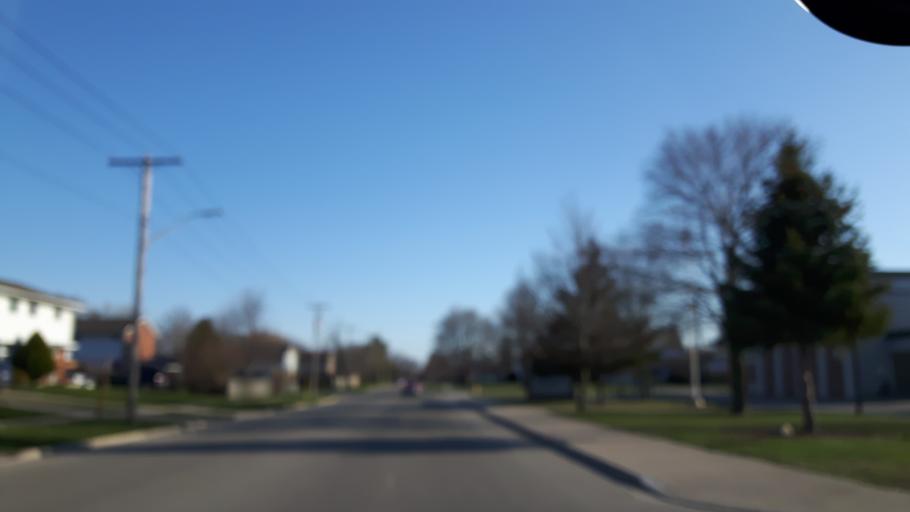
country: CA
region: Ontario
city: Goderich
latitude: 43.7345
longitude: -81.7112
